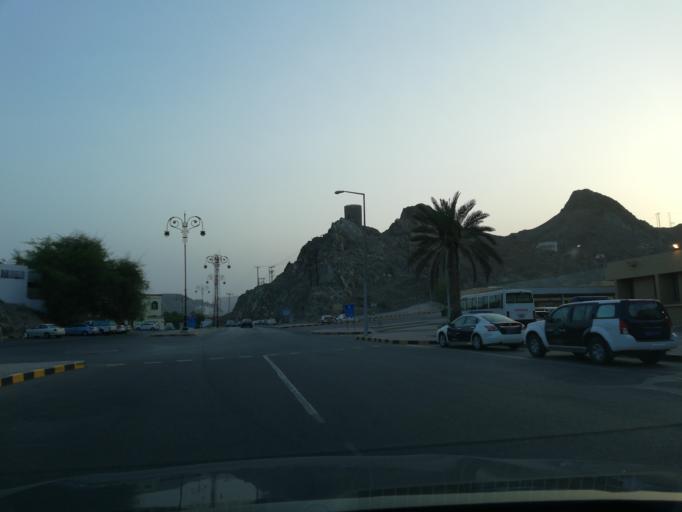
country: OM
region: Muhafazat Masqat
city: Muscat
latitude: 23.6268
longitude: 58.5614
